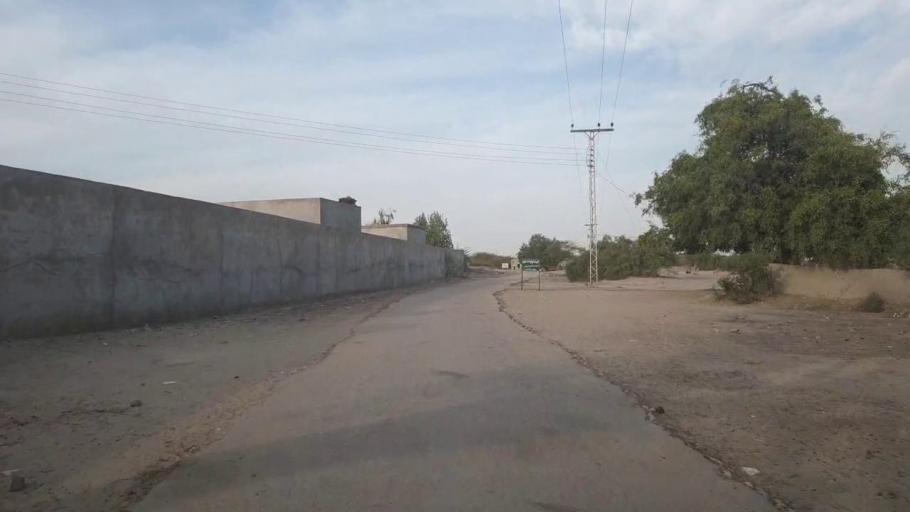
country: PK
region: Sindh
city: Nabisar
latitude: 25.1001
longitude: 69.6735
